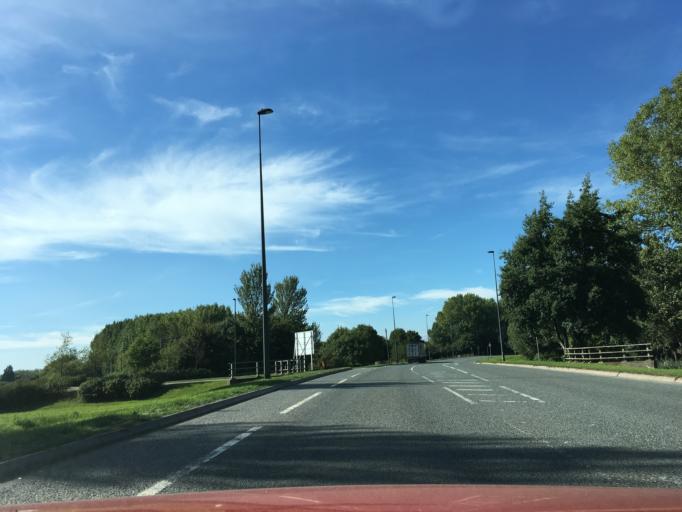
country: GB
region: England
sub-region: South Gloucestershire
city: Severn Beach
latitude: 51.5520
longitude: -2.6526
